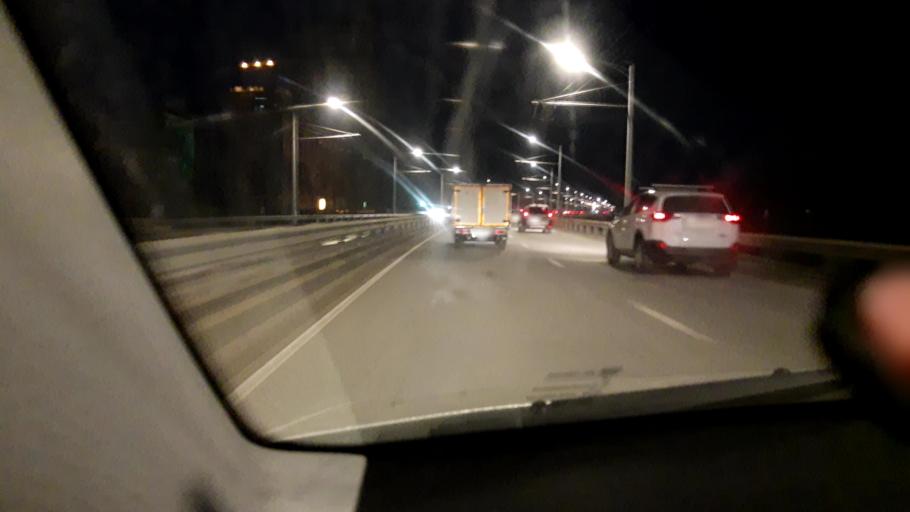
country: RU
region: Bashkortostan
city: Mikhaylovka
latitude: 54.7704
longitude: 55.9073
